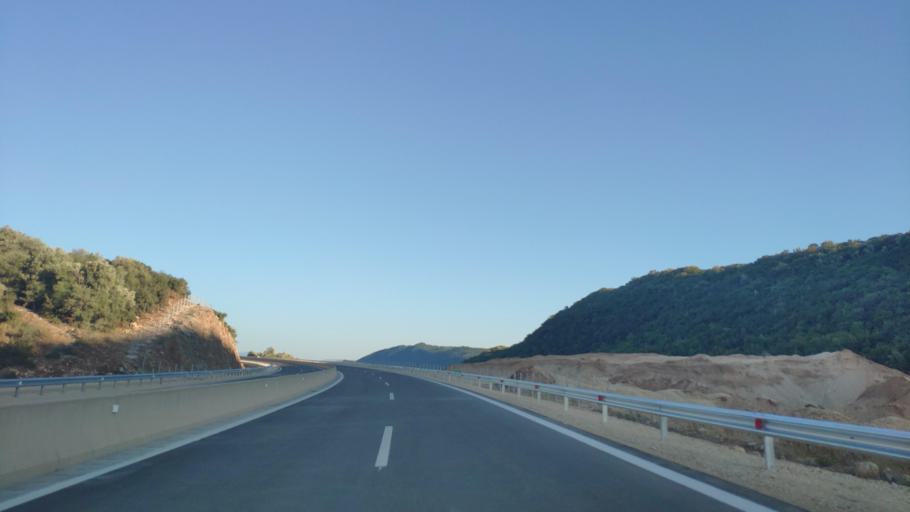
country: GR
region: West Greece
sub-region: Nomos Aitolias kai Akarnanias
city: Katouna
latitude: 38.7841
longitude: 21.1433
